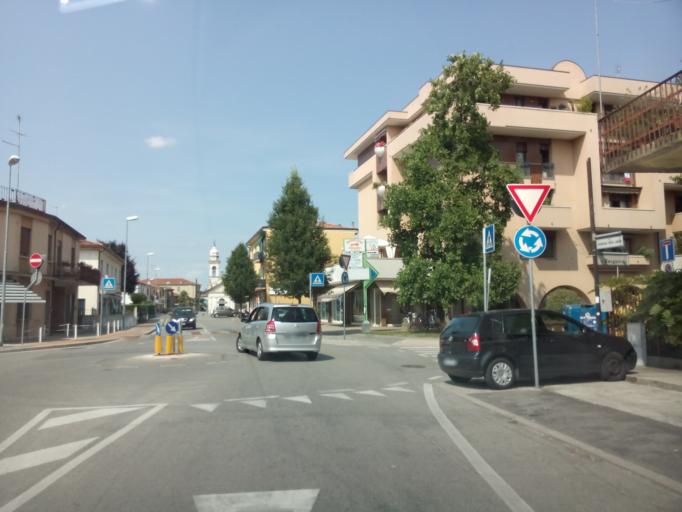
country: IT
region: Veneto
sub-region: Provincia di Padova
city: Cadoneghe
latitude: 45.4234
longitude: 11.9112
